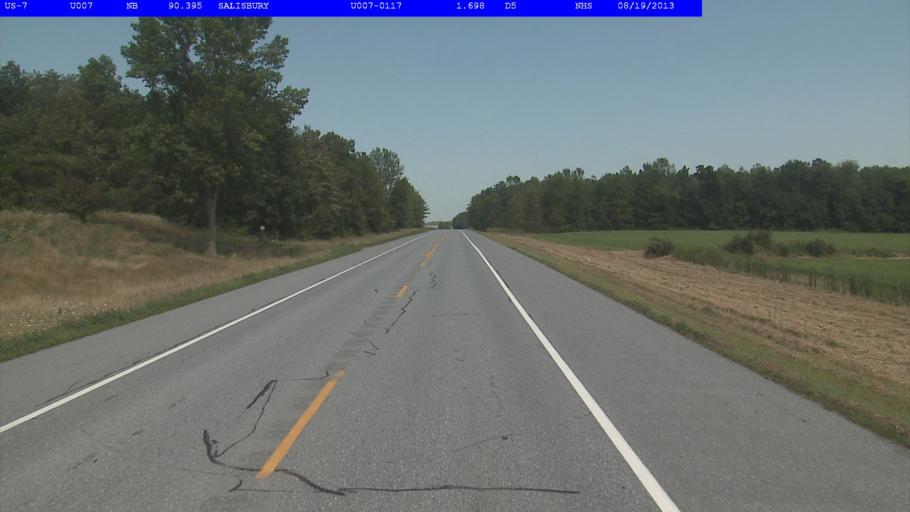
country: US
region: Vermont
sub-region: Addison County
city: Middlebury (village)
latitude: 43.9163
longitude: -73.1115
